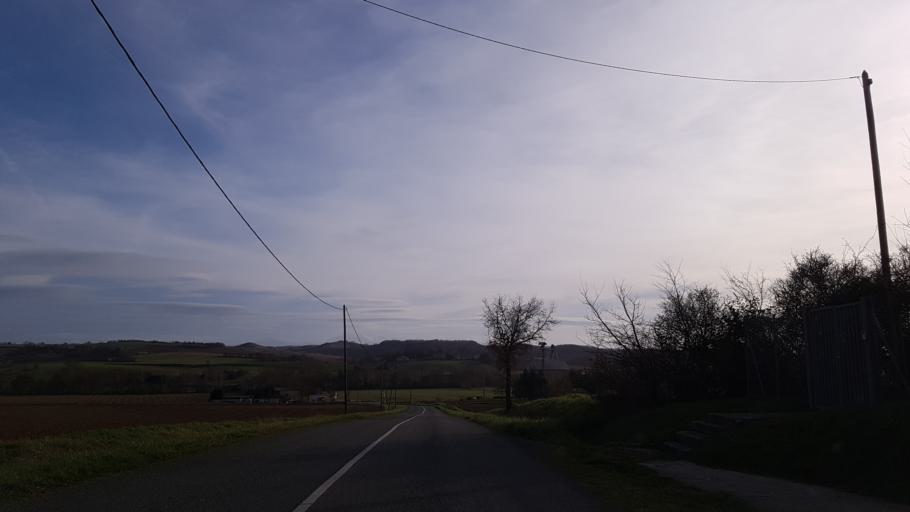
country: FR
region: Languedoc-Roussillon
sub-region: Departement de l'Aude
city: Villeneuve-la-Comptal
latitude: 43.1934
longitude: 1.9038
